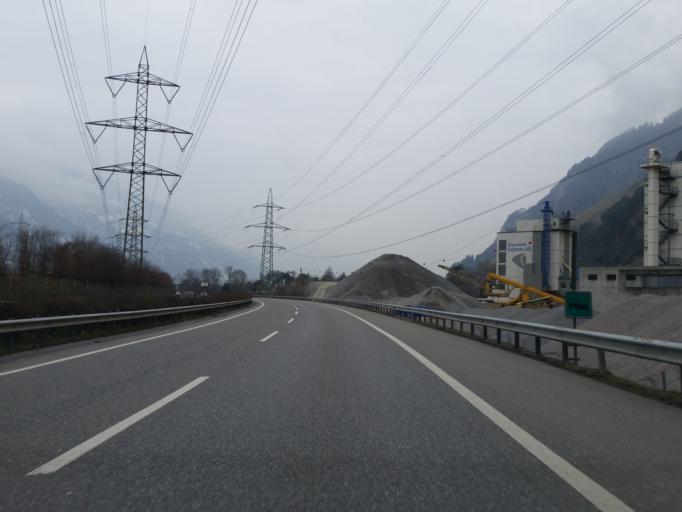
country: CH
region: Grisons
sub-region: Plessur District
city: Chur
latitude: 46.8639
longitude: 9.5117
